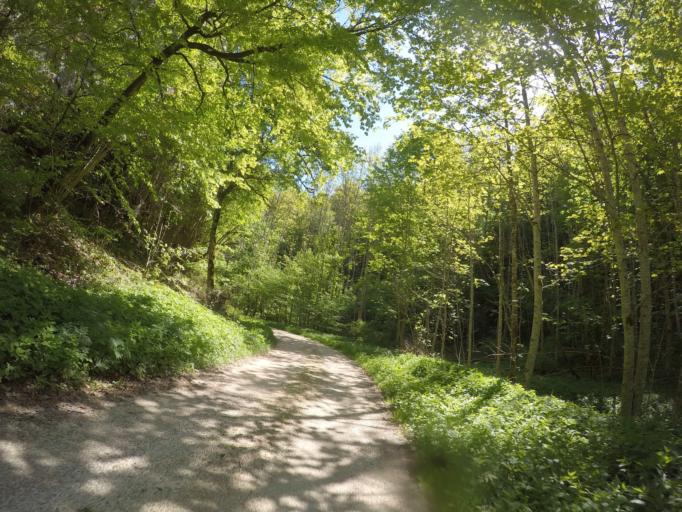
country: DE
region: Baden-Wuerttemberg
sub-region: Tuebingen Region
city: Schelklingen
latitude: 48.4001
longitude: 9.7504
